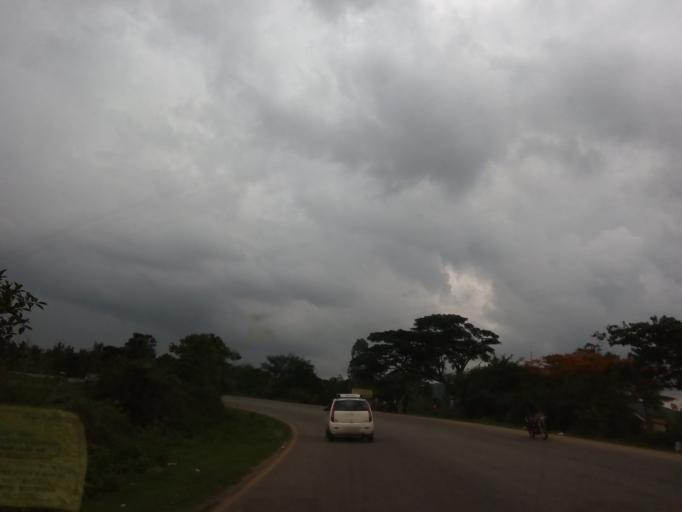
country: IN
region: Karnataka
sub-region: Hassan
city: Hassan
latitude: 13.0827
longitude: 76.0450
